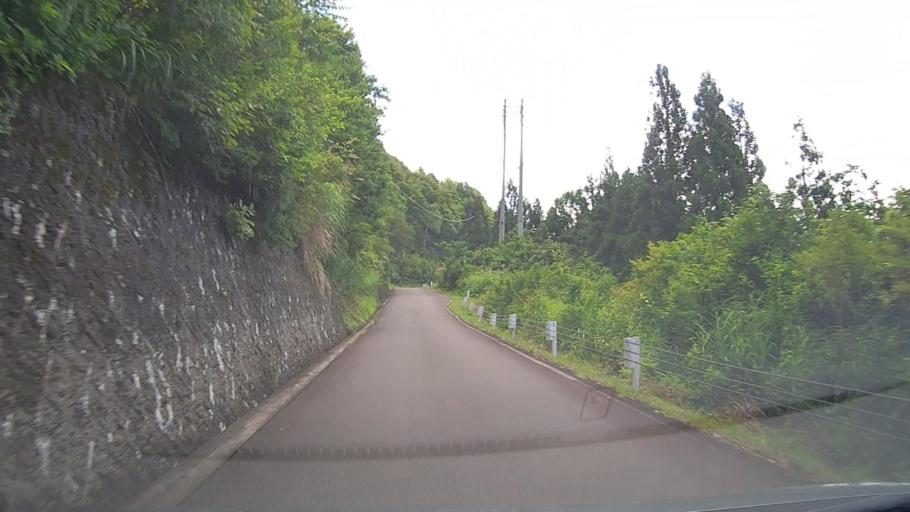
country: JP
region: Nagano
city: Iiyama
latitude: 36.9362
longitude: 138.4612
